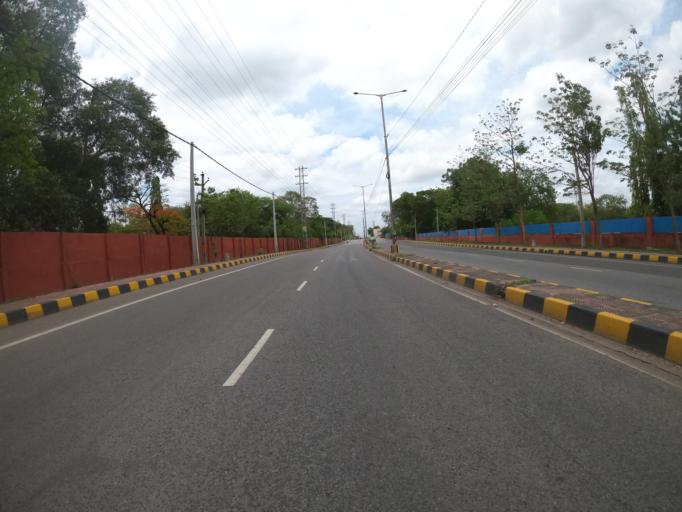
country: IN
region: Telangana
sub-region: Hyderabad
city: Hyderabad
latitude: 17.3764
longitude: 78.3913
